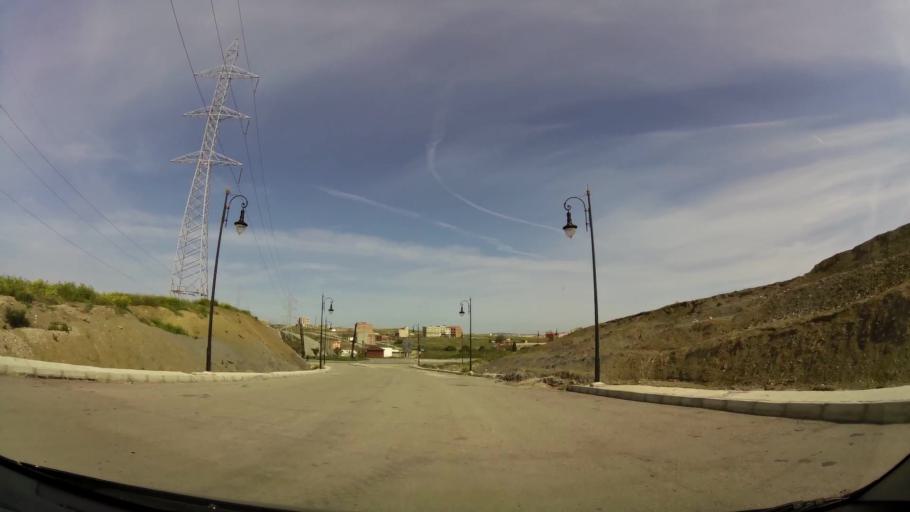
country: MA
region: Tanger-Tetouan
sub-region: Tanger-Assilah
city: Tangier
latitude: 35.7057
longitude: -5.8130
